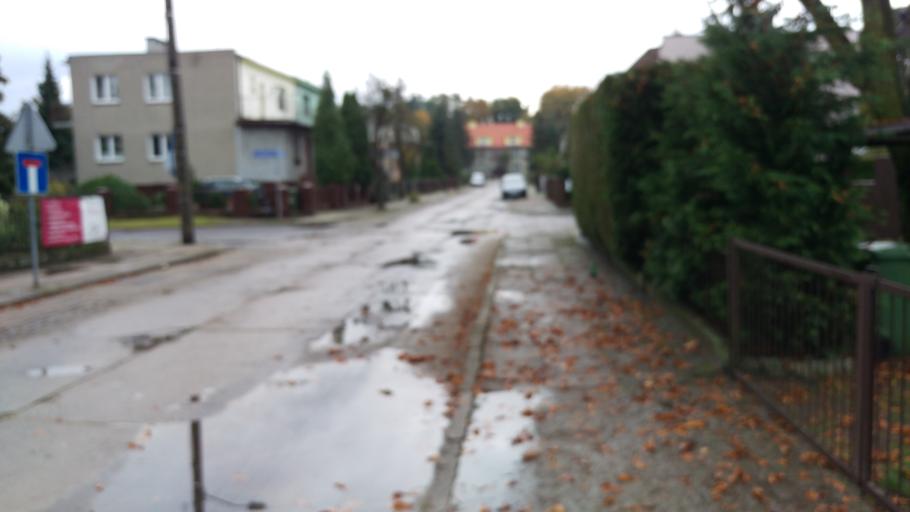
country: PL
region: West Pomeranian Voivodeship
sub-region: Szczecin
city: Szczecin
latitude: 53.4020
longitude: 14.6847
